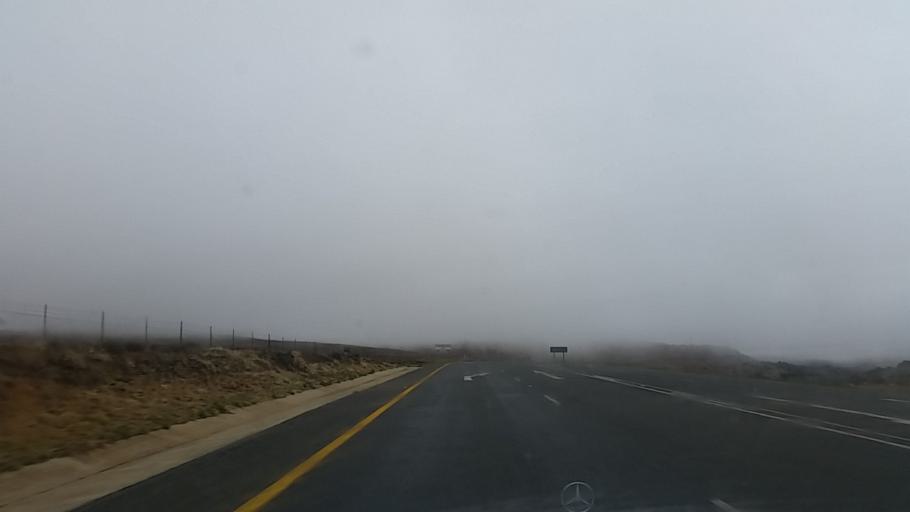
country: ZA
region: Eastern Cape
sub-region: Cacadu District Municipality
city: Graaff-Reinet
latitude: -31.9532
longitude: 24.7264
